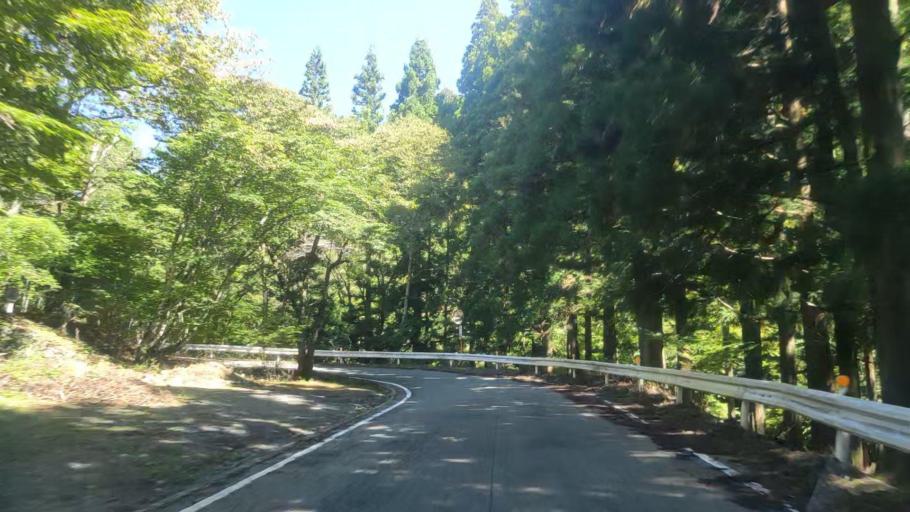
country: JP
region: Yamanashi
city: Fujikawaguchiko
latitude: 35.5527
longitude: 138.7868
